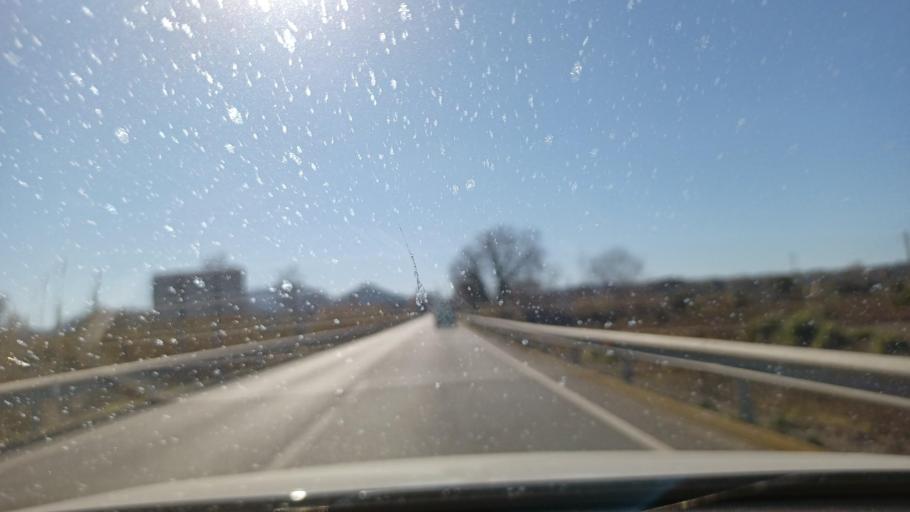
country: ES
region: Catalonia
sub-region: Provincia de Tarragona
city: Amposta
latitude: 40.7183
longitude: 0.5854
